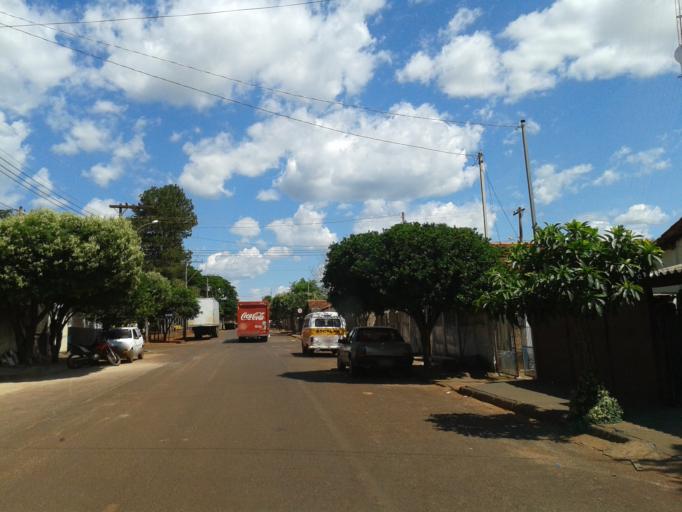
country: BR
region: Minas Gerais
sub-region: Centralina
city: Centralina
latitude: -18.7212
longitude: -49.1962
